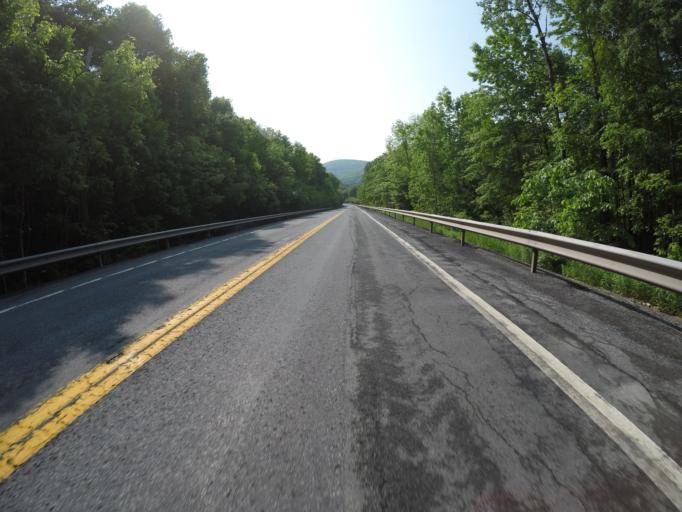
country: US
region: New York
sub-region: Sullivan County
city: Livingston Manor
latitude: 42.1265
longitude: -74.7079
